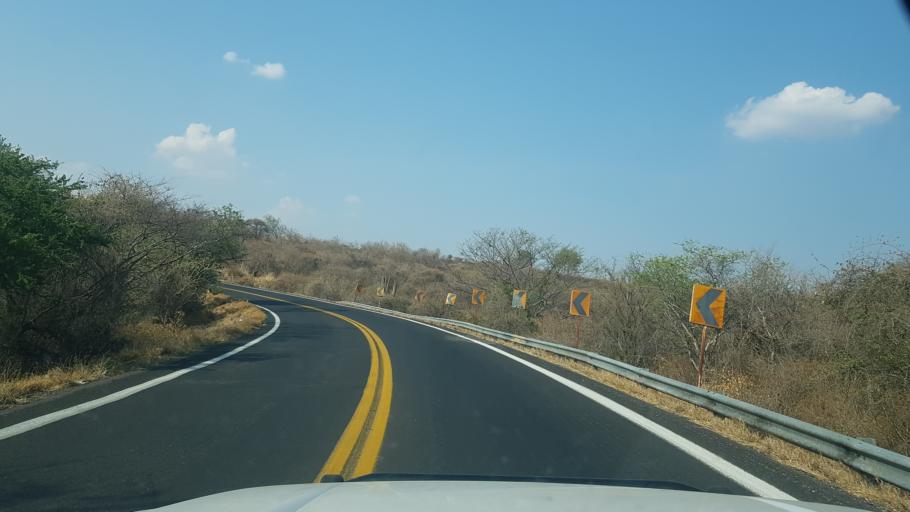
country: MX
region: Puebla
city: Calmeca
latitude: 18.6508
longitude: -98.6644
